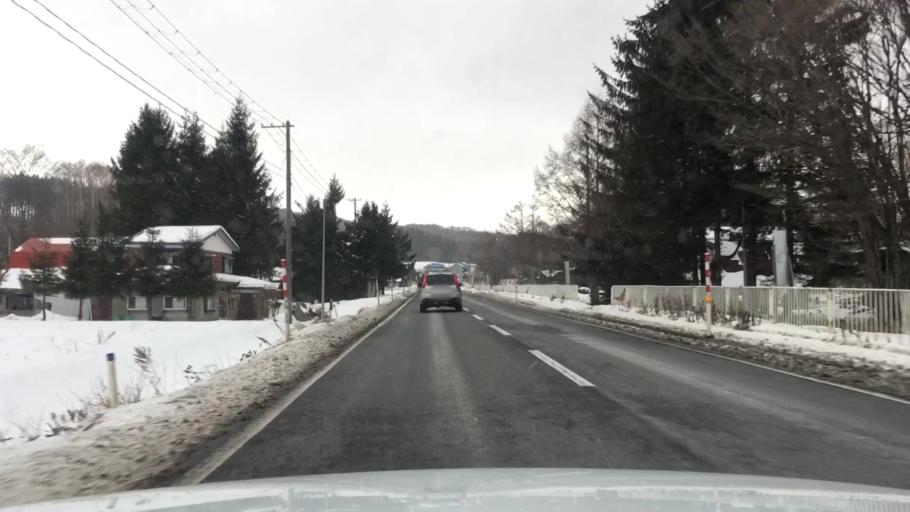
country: JP
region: Iwate
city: Morioka-shi
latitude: 39.6470
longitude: 141.3616
